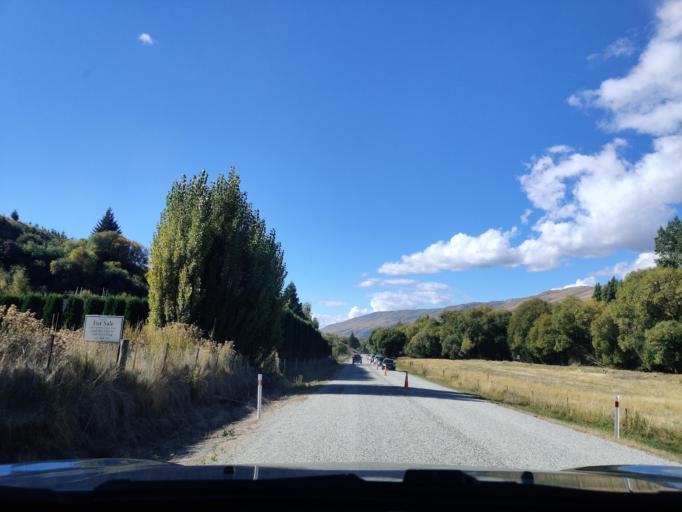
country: NZ
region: Otago
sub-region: Queenstown-Lakes District
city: Arrowtown
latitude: -44.8745
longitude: 169.0098
